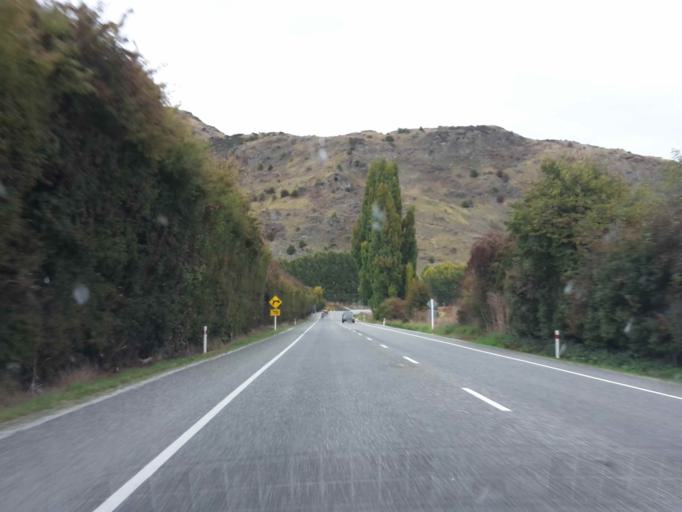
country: NZ
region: Otago
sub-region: Queenstown-Lakes District
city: Arrowtown
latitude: -44.9806
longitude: 168.8421
